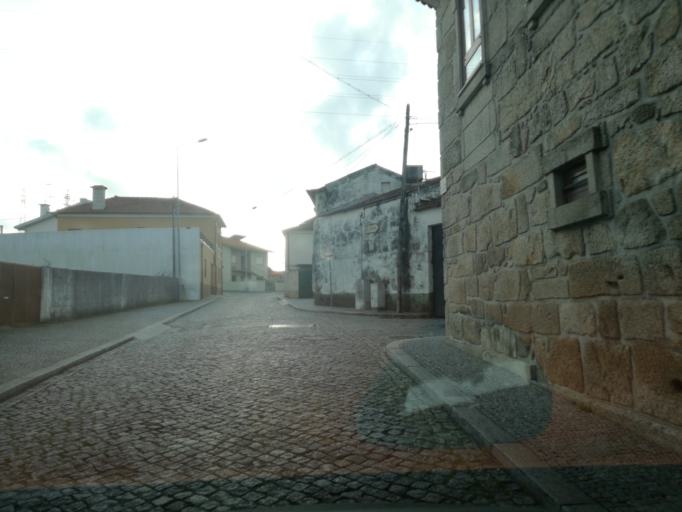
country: PT
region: Porto
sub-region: Maia
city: Maia
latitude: 41.2412
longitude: -8.6120
